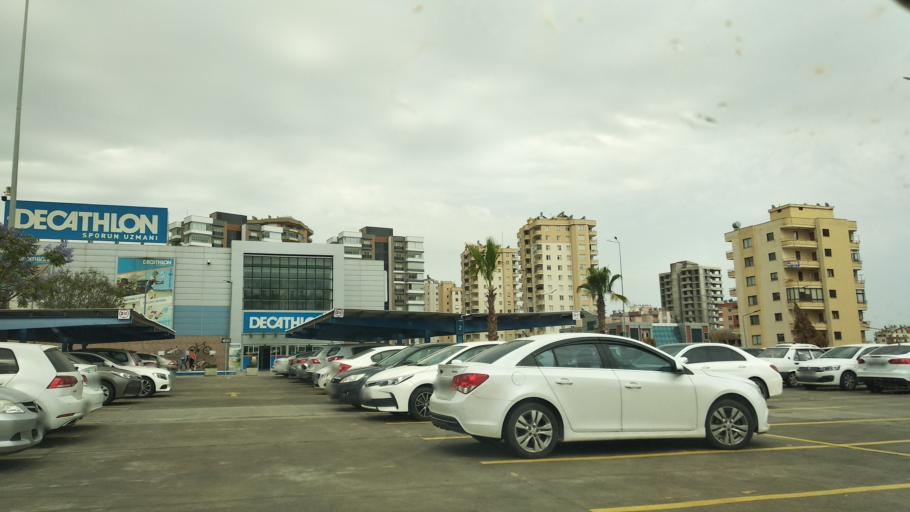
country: TR
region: Mersin
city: Mercin
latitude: 36.7996
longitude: 34.5951
